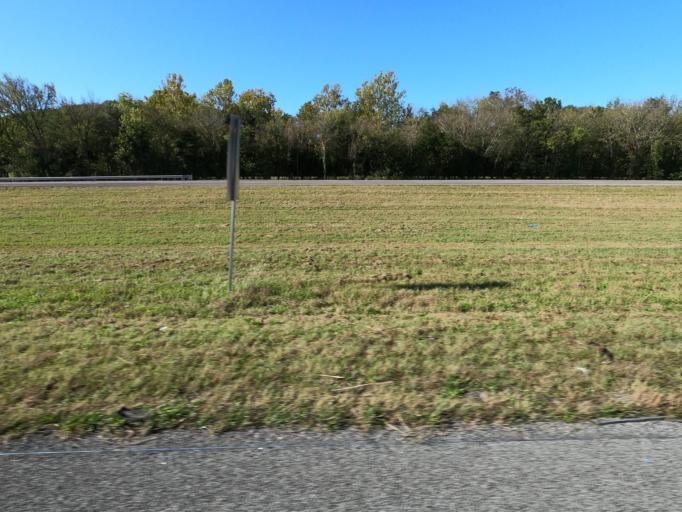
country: US
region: Tennessee
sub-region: Rutherford County
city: Plainview
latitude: 35.6643
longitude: -86.2741
